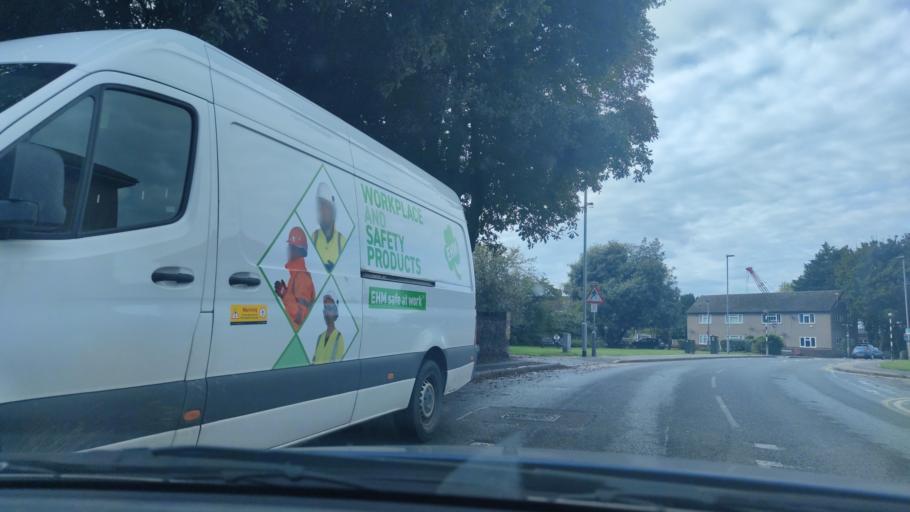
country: GB
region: England
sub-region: Borough of Thurrock
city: Grays
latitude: 51.4761
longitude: 0.3404
